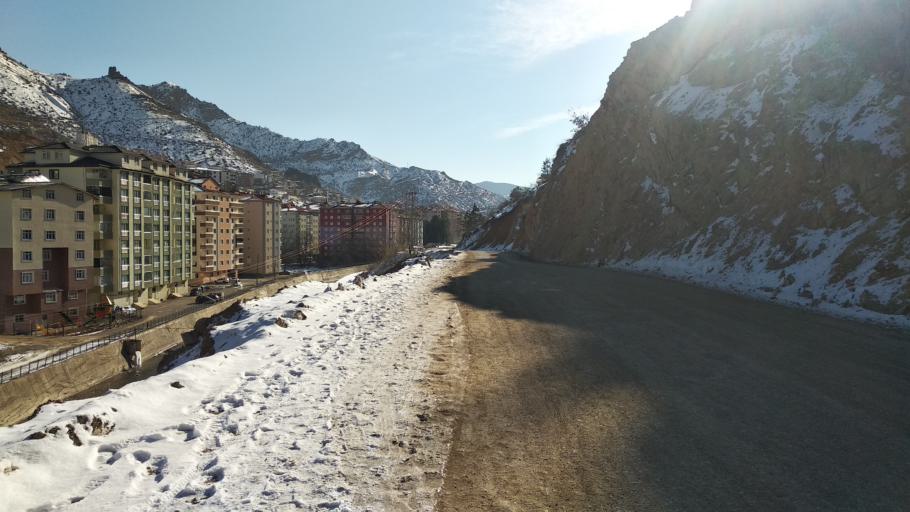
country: TR
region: Gumushane
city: Gumushkhane
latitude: 40.4536
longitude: 39.4896
